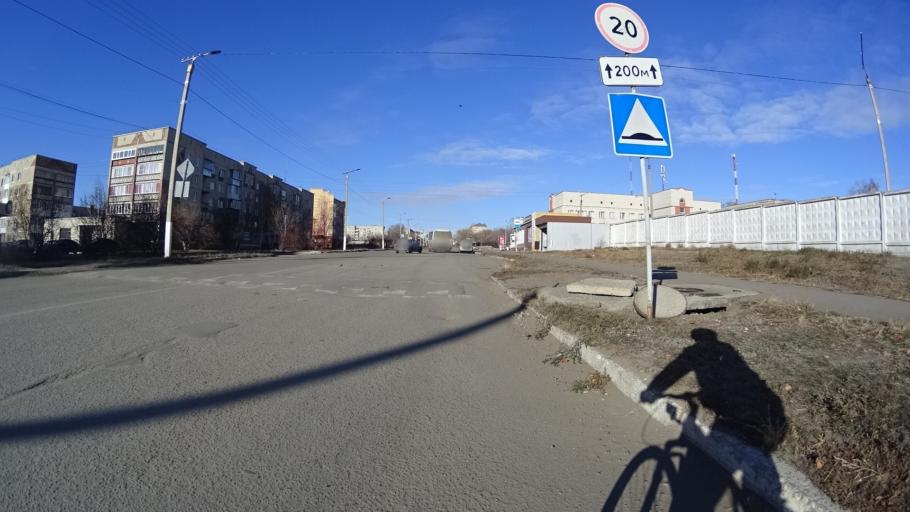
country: RU
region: Chelyabinsk
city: Troitsk
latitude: 54.0746
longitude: 61.5334
